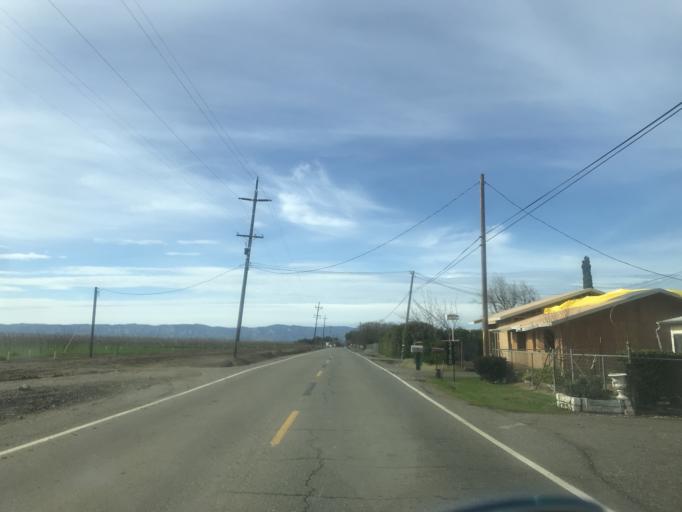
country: US
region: California
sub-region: Yolo County
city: Cottonwood
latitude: 38.6635
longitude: -121.8735
